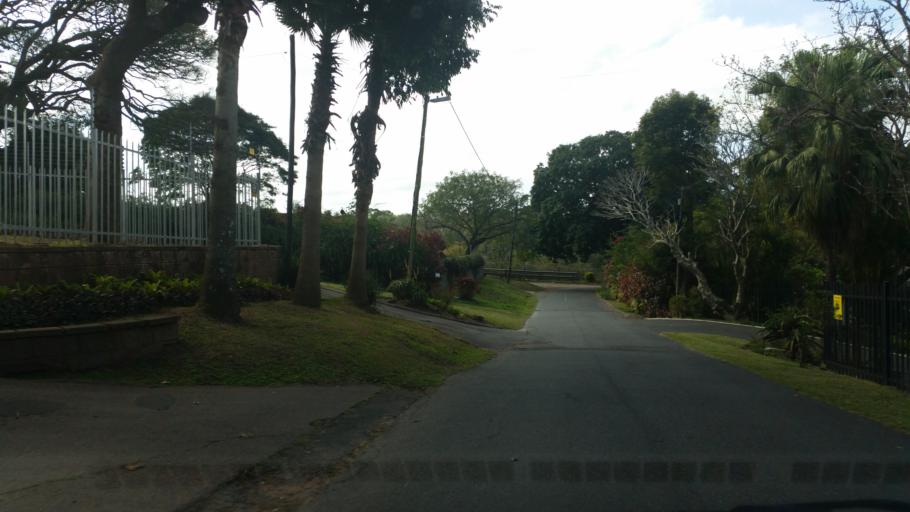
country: ZA
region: KwaZulu-Natal
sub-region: eThekwini Metropolitan Municipality
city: Berea
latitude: -29.8365
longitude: 30.8970
